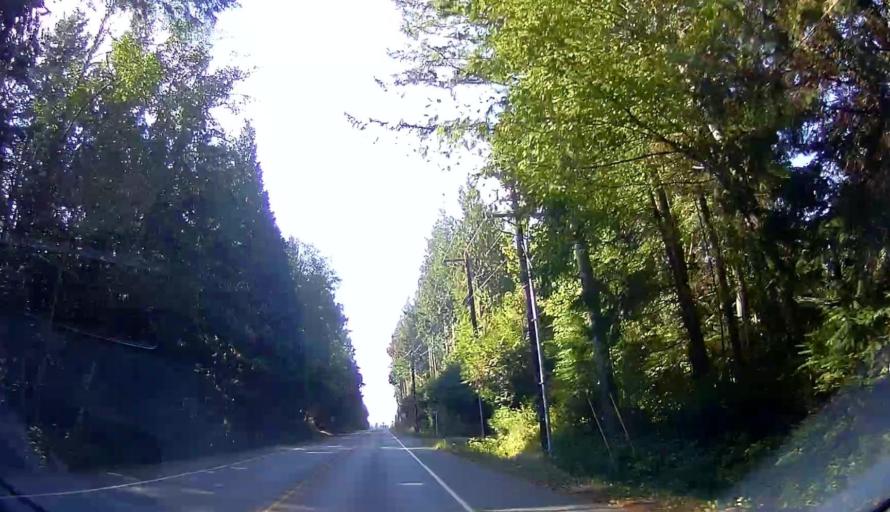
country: US
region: Washington
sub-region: Island County
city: Camano
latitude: 48.2257
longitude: -122.5142
